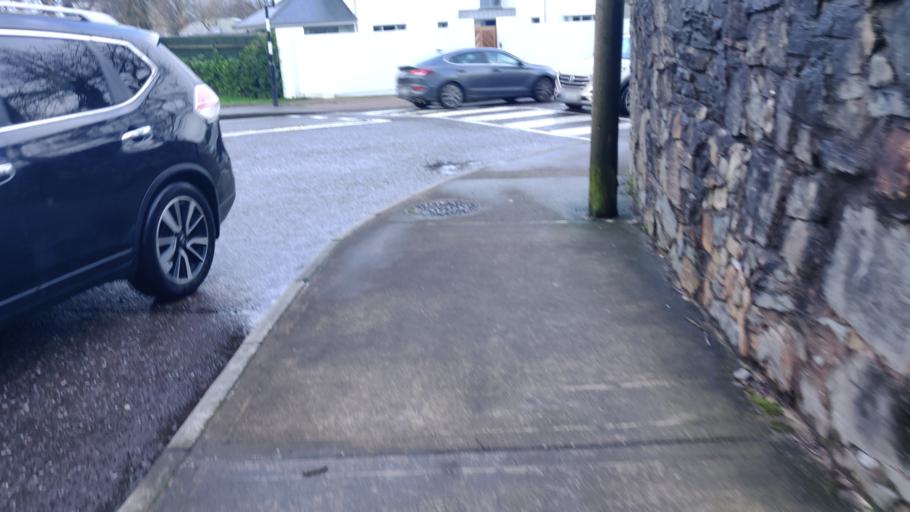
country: IE
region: Munster
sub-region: County Cork
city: Cork
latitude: 51.8761
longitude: -8.4314
